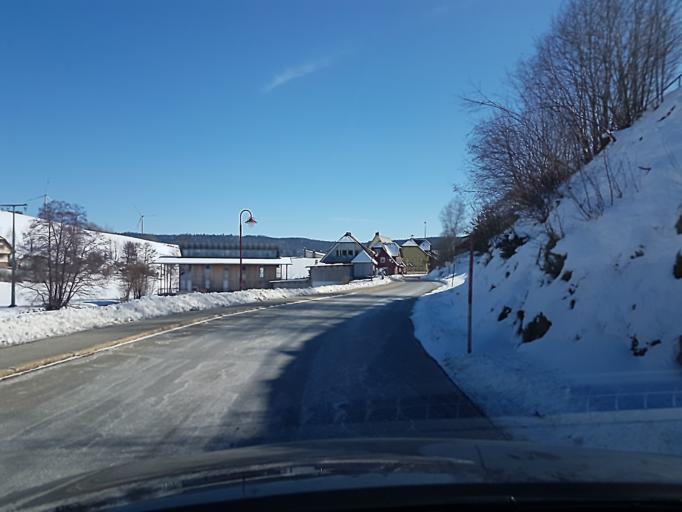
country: DE
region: Baden-Wuerttemberg
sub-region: Freiburg Region
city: Sankt Georgen im Schwarzwald
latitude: 48.1622
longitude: 8.3134
